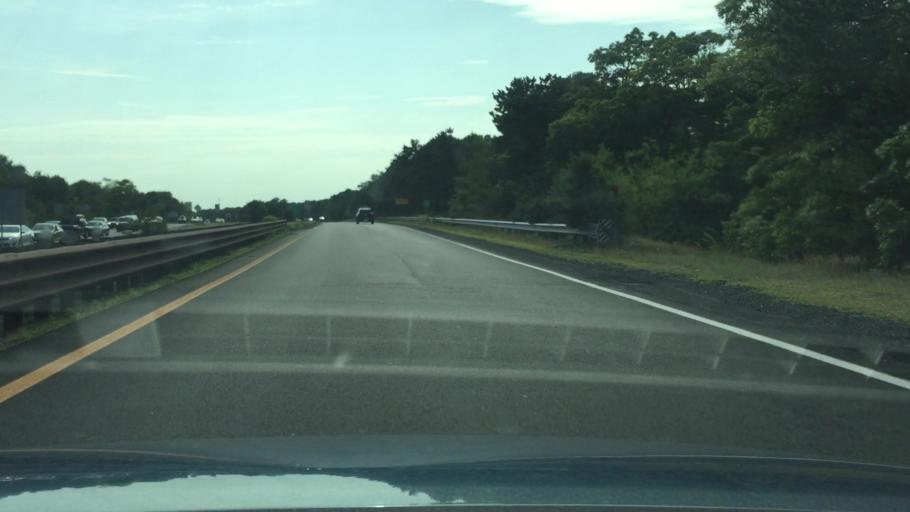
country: US
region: Massachusetts
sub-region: Barnstable County
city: South Dennis
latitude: 41.6998
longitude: -70.1453
